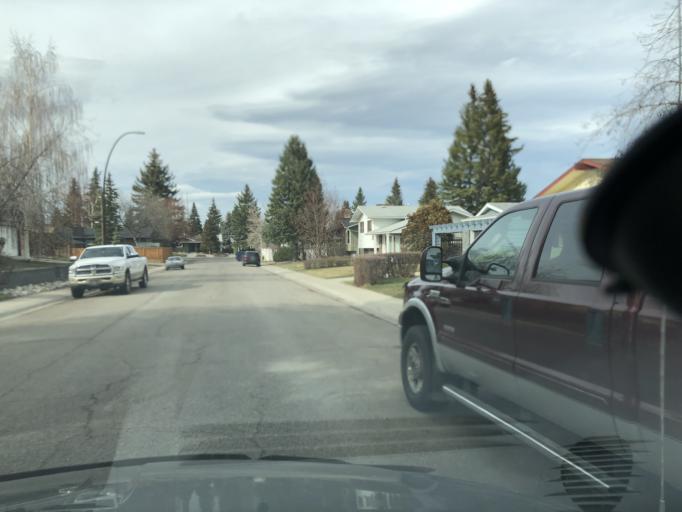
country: CA
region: Alberta
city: Calgary
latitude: 50.9355
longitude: -114.0389
